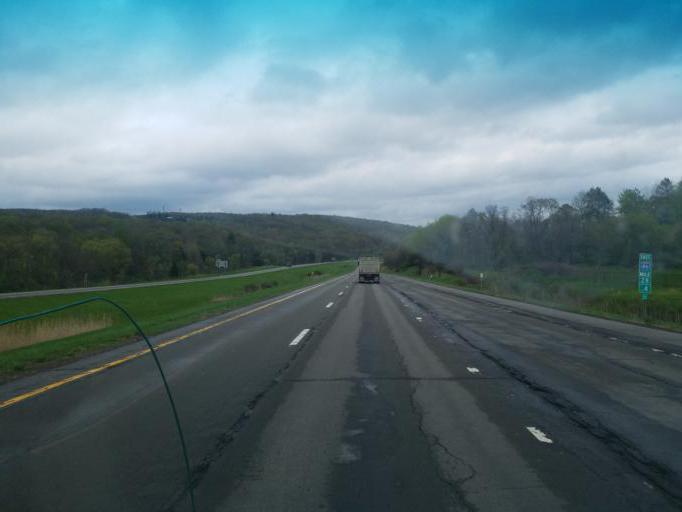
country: US
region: New York
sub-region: Chautauqua County
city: Jamestown
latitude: 42.1224
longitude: -79.2352
